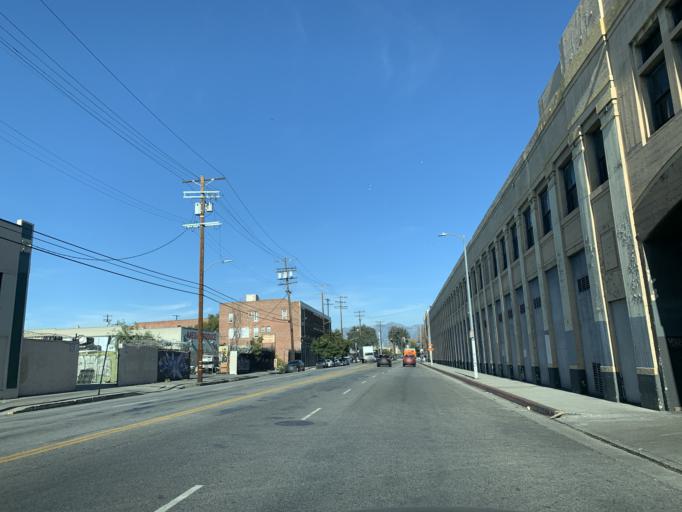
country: US
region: California
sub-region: Los Angeles County
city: Los Angeles
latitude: 34.0356
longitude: -118.2419
